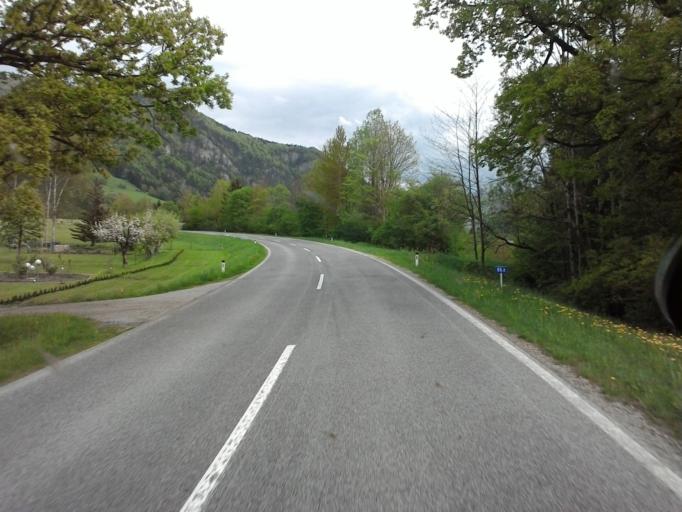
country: AT
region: Styria
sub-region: Politischer Bezirk Liezen
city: Landl
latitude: 47.6893
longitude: 14.6974
